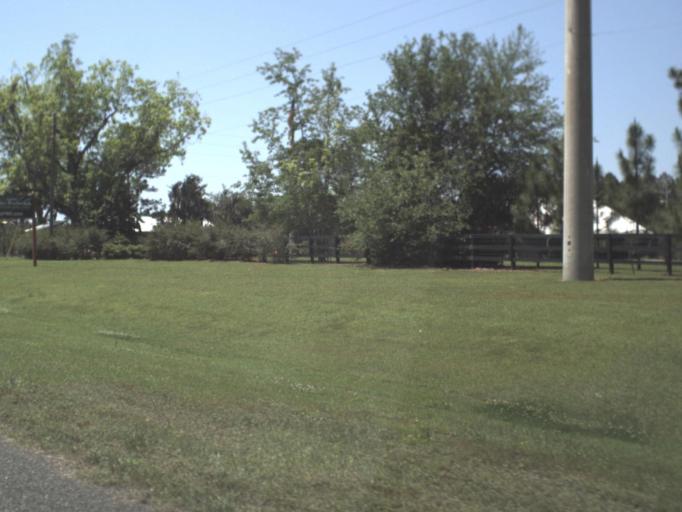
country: US
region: Florida
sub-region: Jefferson County
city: Monticello
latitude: 30.4183
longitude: -83.9111
